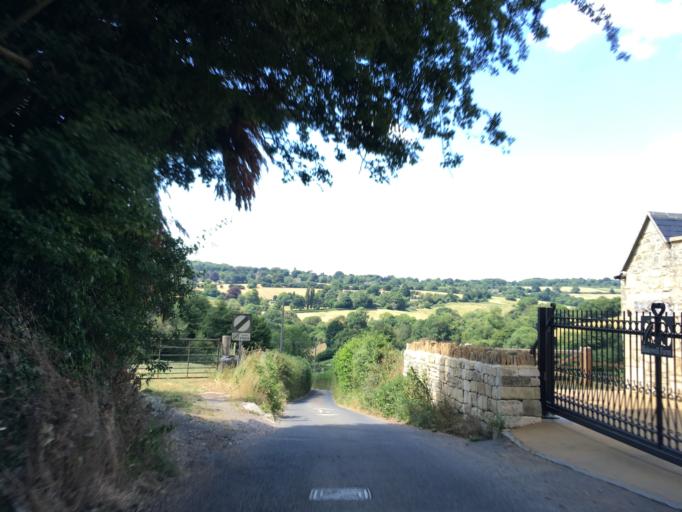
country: GB
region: England
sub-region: Gloucestershire
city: Painswick
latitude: 51.7866
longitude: -2.2015
